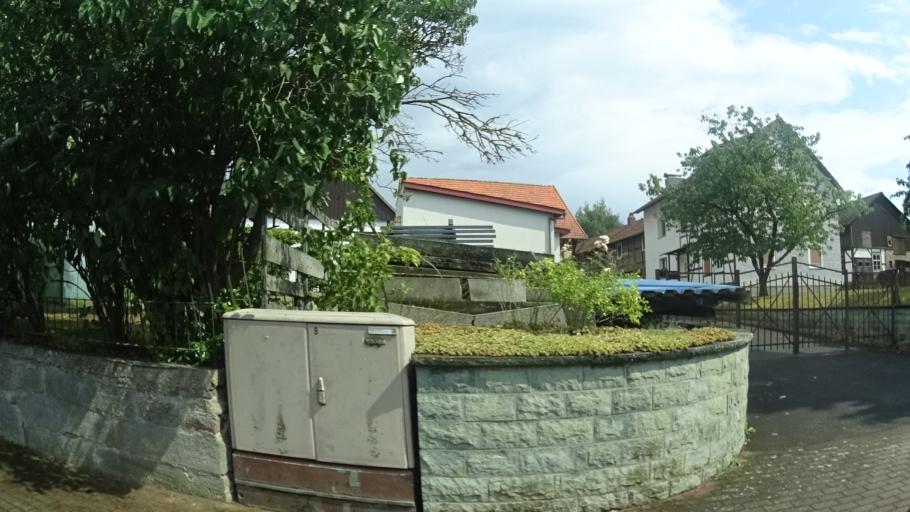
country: DE
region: Hesse
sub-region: Regierungsbezirk Kassel
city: Niederaula
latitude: 50.7940
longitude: 9.6186
